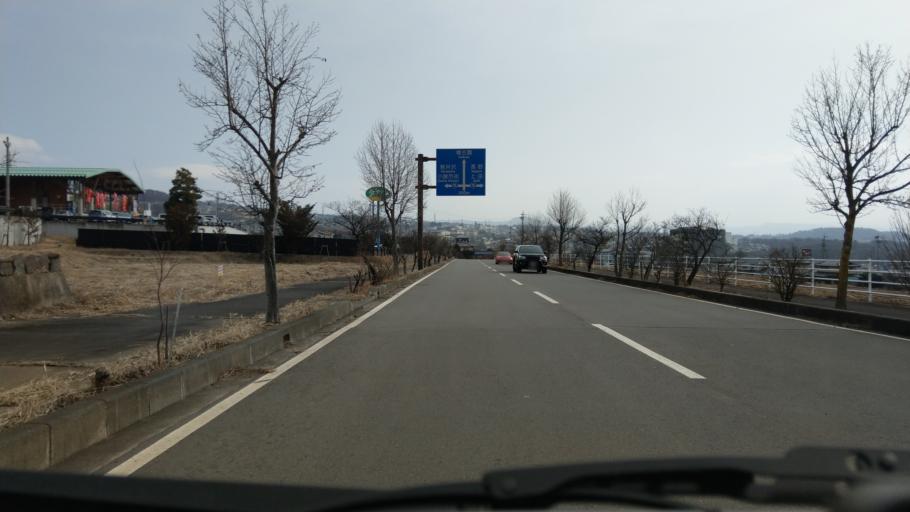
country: JP
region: Nagano
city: Komoro
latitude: 36.3387
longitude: 138.4077
